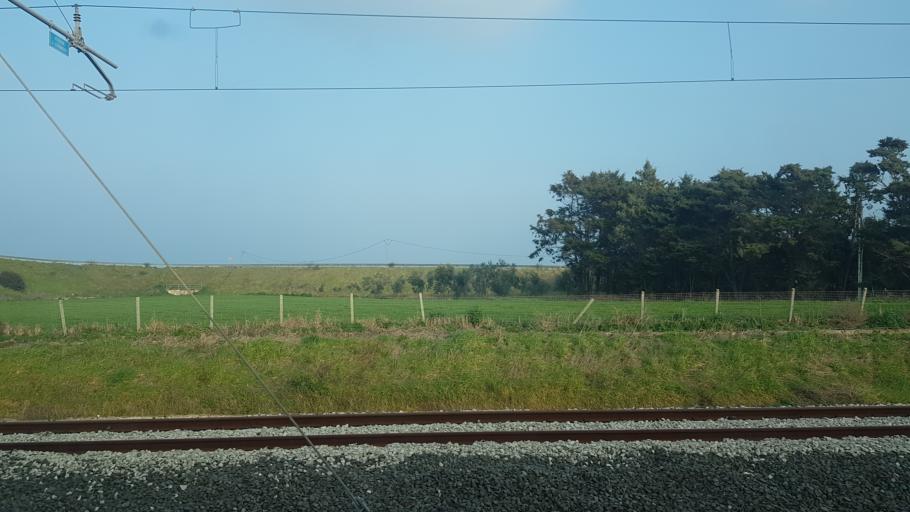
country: IT
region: Apulia
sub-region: Provincia di Foggia
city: Lesina
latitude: 41.8567
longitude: 15.2961
